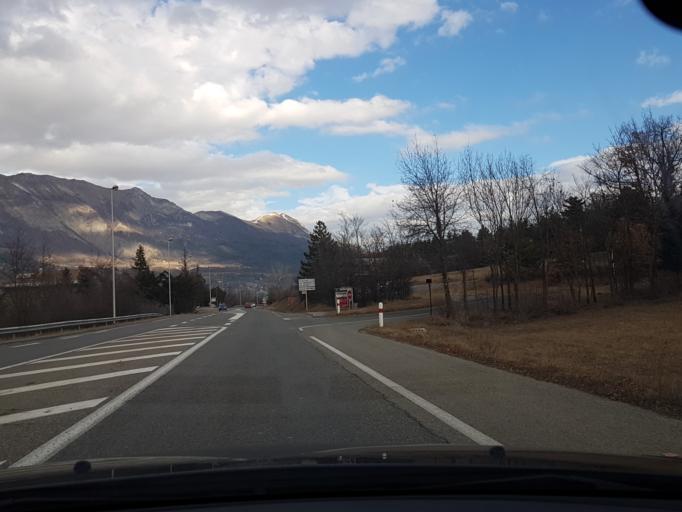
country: FR
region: Provence-Alpes-Cote d'Azur
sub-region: Departement des Hautes-Alpes
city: Gap
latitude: 44.5283
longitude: 6.0481
